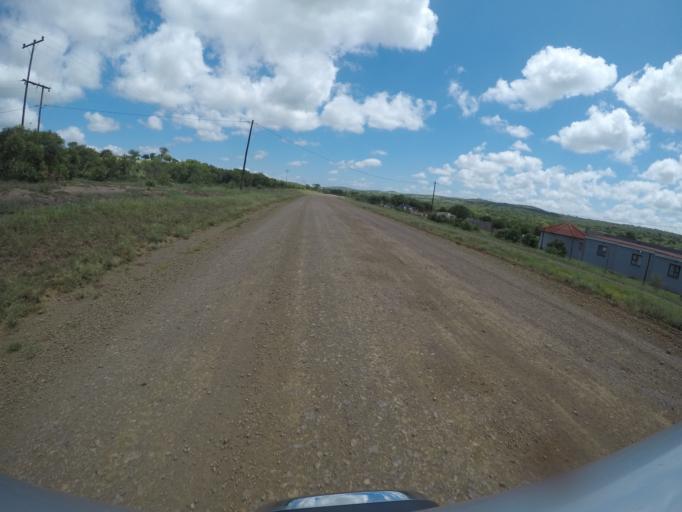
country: ZA
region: KwaZulu-Natal
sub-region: uThungulu District Municipality
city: Empangeni
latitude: -28.5922
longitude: 31.8389
